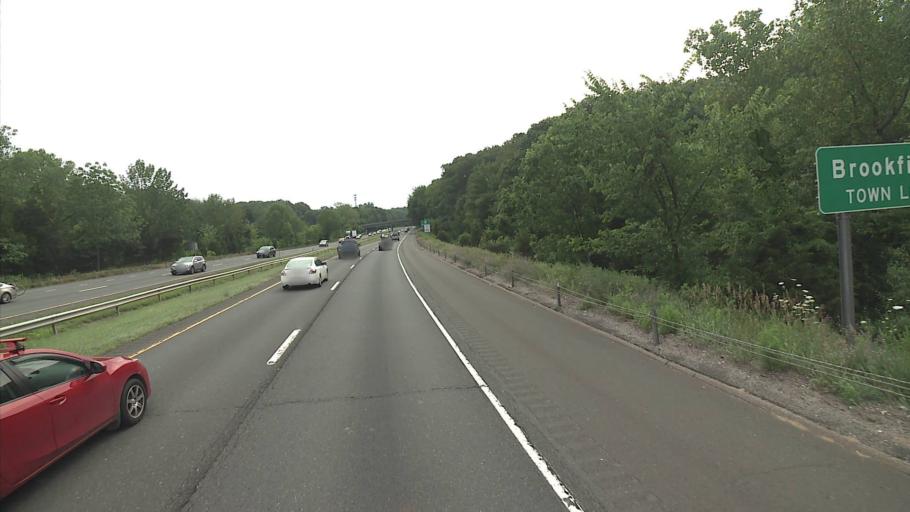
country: US
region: Connecticut
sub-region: Fairfield County
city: Bethel
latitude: 41.4239
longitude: -73.3813
